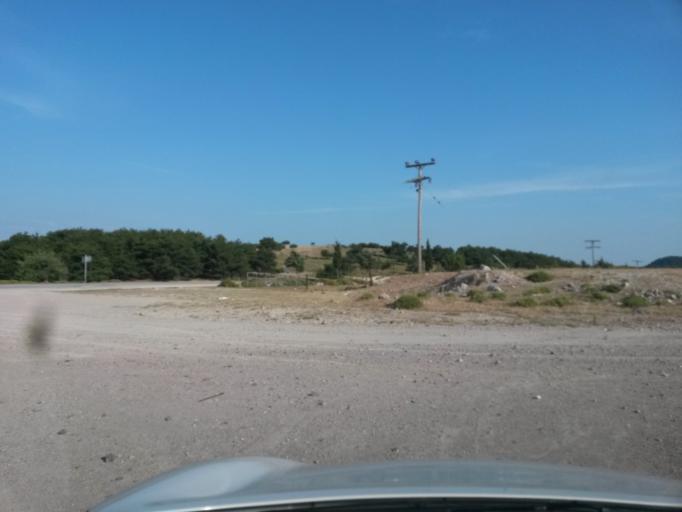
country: GR
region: North Aegean
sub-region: Nomos Lesvou
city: Mantamados
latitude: 39.3426
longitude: 26.3185
